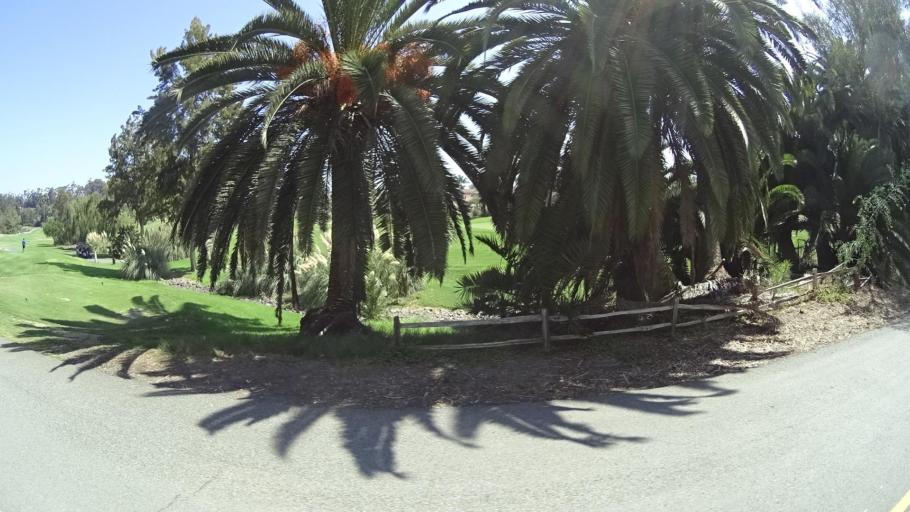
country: US
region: California
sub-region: San Diego County
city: Fairbanks Ranch
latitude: 32.9921
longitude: -117.2168
